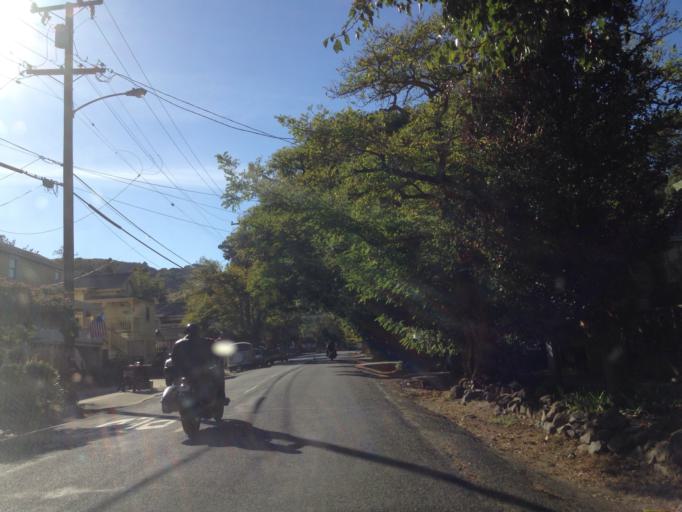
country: US
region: California
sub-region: Contra Costa County
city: Crockett
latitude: 38.0453
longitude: -122.1865
